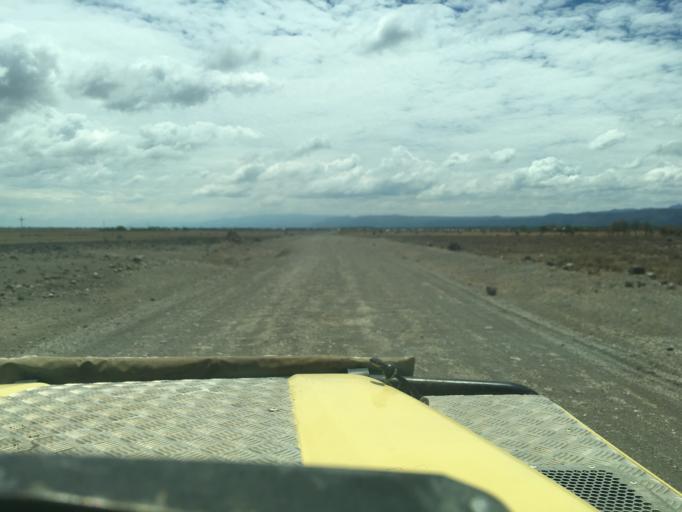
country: TZ
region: Arusha
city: Mto wa Mbu
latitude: -3.3462
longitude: 35.9112
